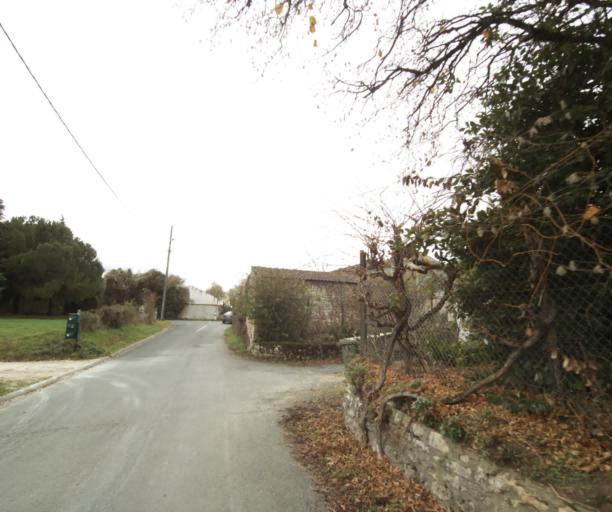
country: FR
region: Poitou-Charentes
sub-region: Departement de la Charente-Maritime
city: Corme-Royal
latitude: 45.7393
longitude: -0.8254
